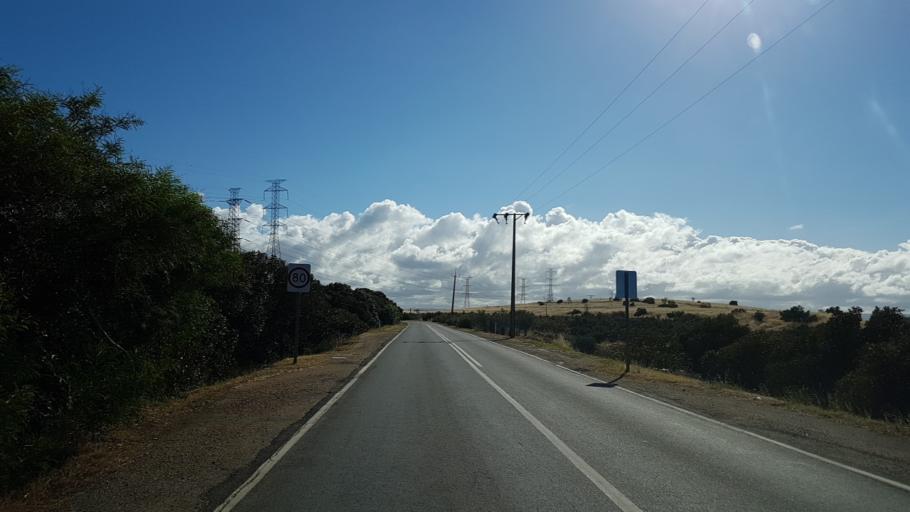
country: AU
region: South Australia
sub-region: Port Adelaide Enfield
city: Birkenhead
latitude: -34.8098
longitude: 138.5260
